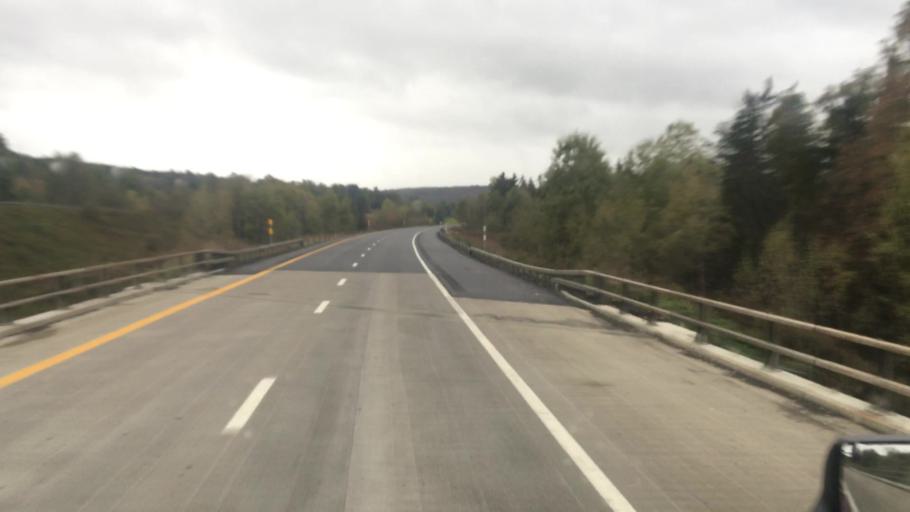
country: US
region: New York
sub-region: Chenango County
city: Bainbridge
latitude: 42.2065
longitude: -75.5212
